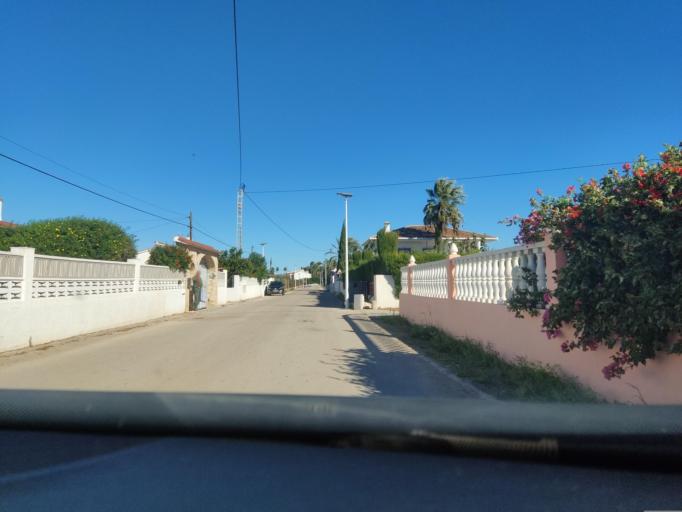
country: ES
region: Valencia
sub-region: Provincia de Alicante
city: els Poblets
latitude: 38.8550
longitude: 0.0273
